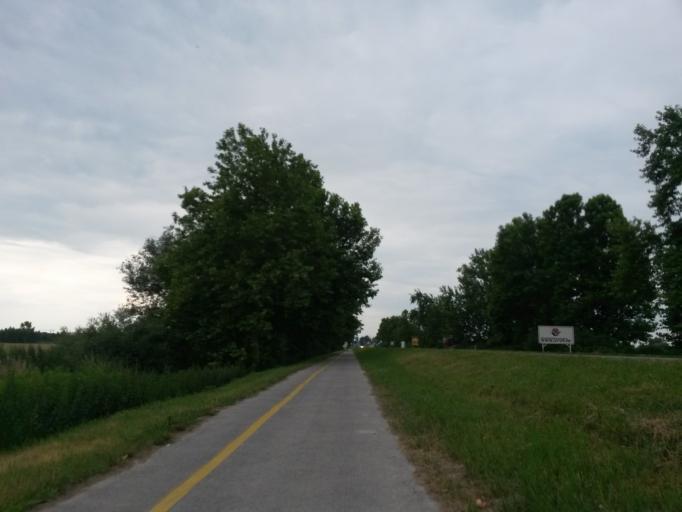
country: HR
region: Osjecko-Baranjska
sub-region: Grad Osijek
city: Osijek
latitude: 45.5729
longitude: 18.7135
